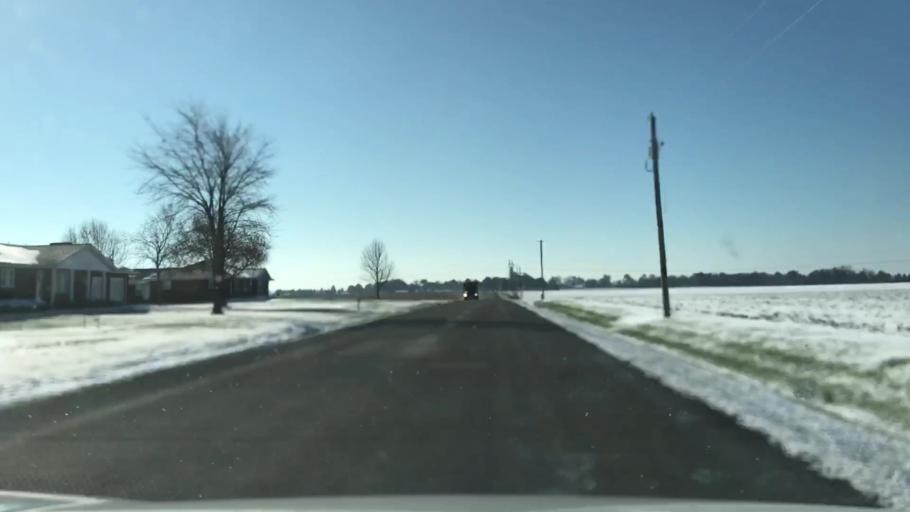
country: US
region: Illinois
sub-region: Washington County
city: Okawville
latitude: 38.4068
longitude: -89.4865
